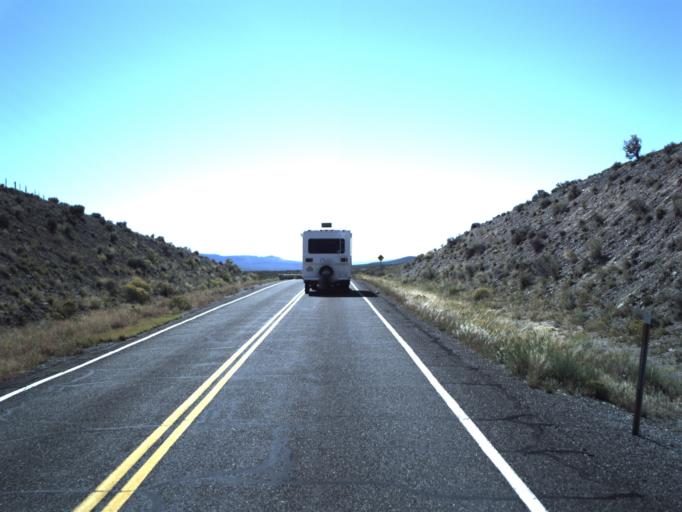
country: US
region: Utah
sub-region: Piute County
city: Junction
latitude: 38.3447
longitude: -111.9523
